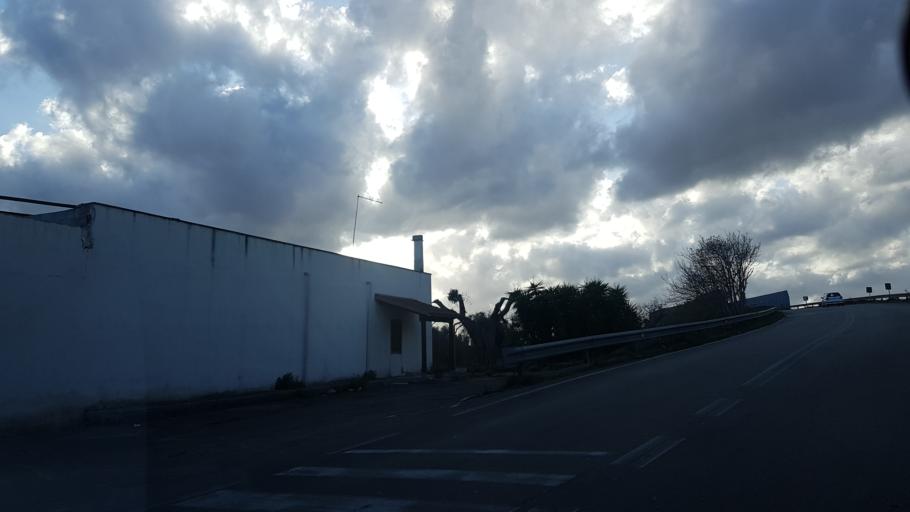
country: IT
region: Apulia
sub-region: Provincia di Brindisi
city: Torchiarolo
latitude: 40.4867
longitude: 18.0427
